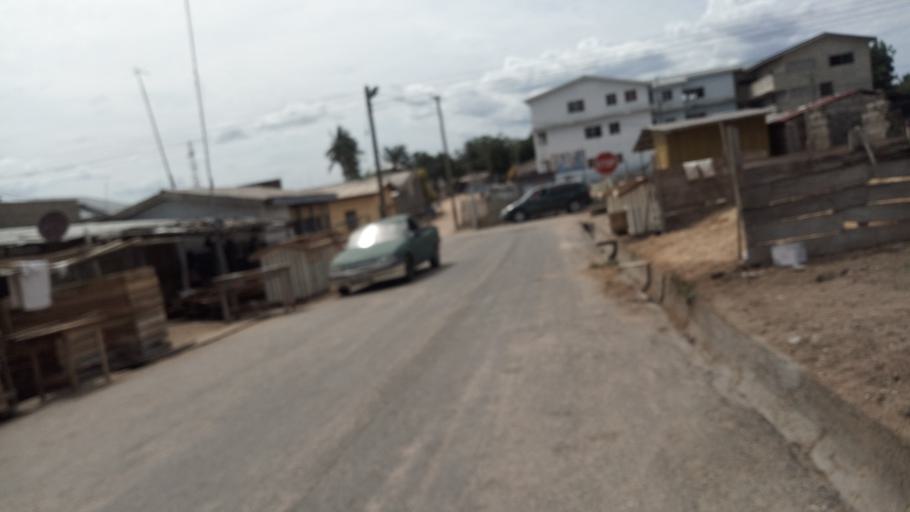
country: GH
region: Central
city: Winneba
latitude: 5.3488
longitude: -0.6247
